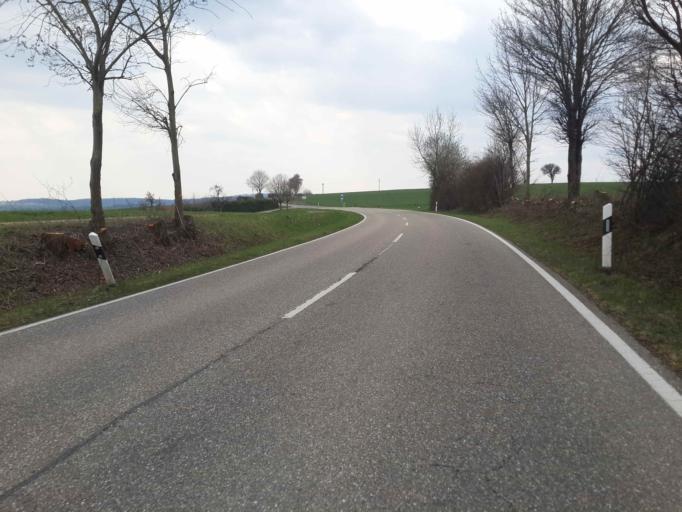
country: DE
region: Baden-Wuerttemberg
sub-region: Regierungsbezirk Stuttgart
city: Eppingen
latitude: 49.1768
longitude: 8.8787
